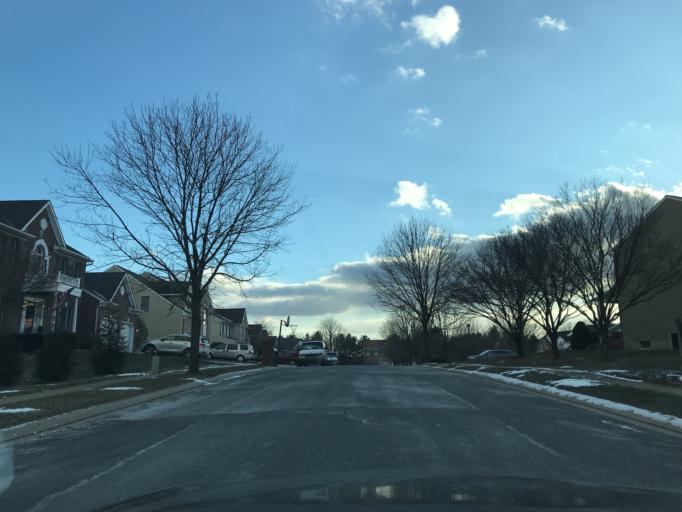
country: US
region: Maryland
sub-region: Harford County
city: Bel Air North
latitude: 39.5808
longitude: -76.3836
